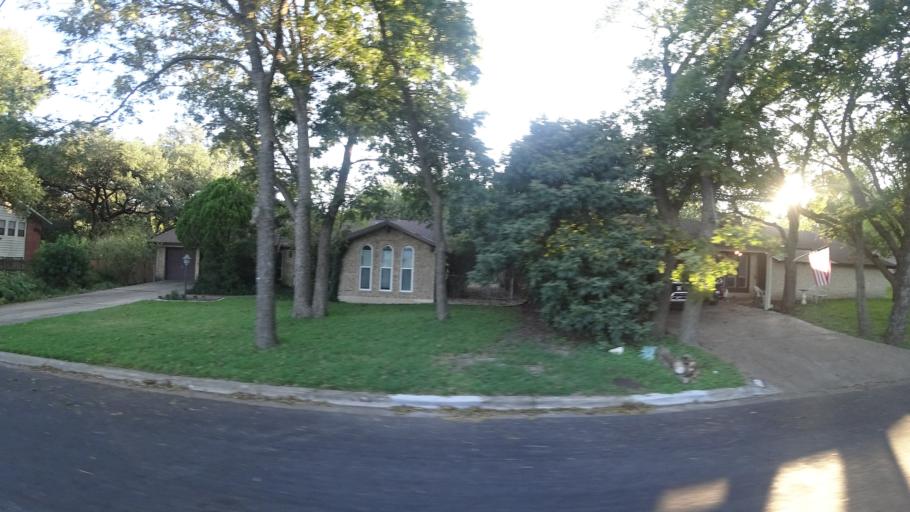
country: US
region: Texas
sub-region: Travis County
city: Wells Branch
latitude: 30.3675
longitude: -97.6743
